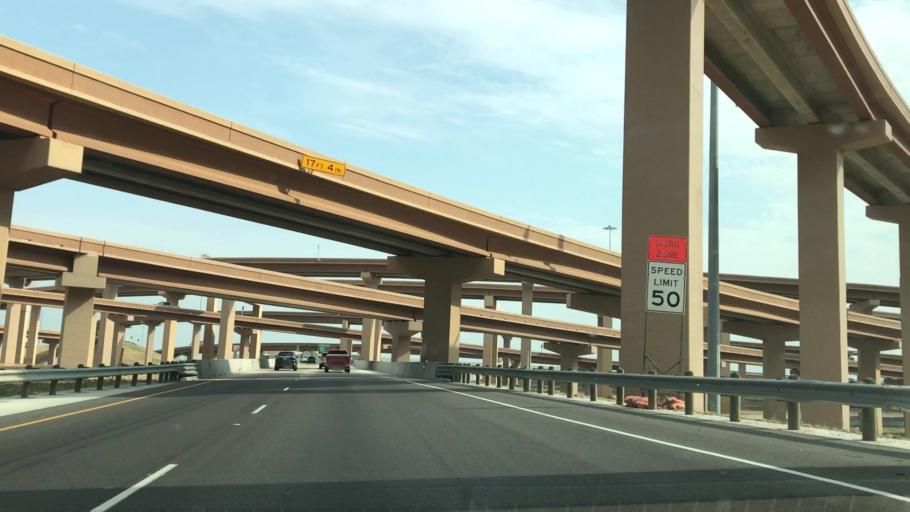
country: US
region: Texas
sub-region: Tarrant County
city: Blue Mound
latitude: 32.8379
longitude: -97.3114
